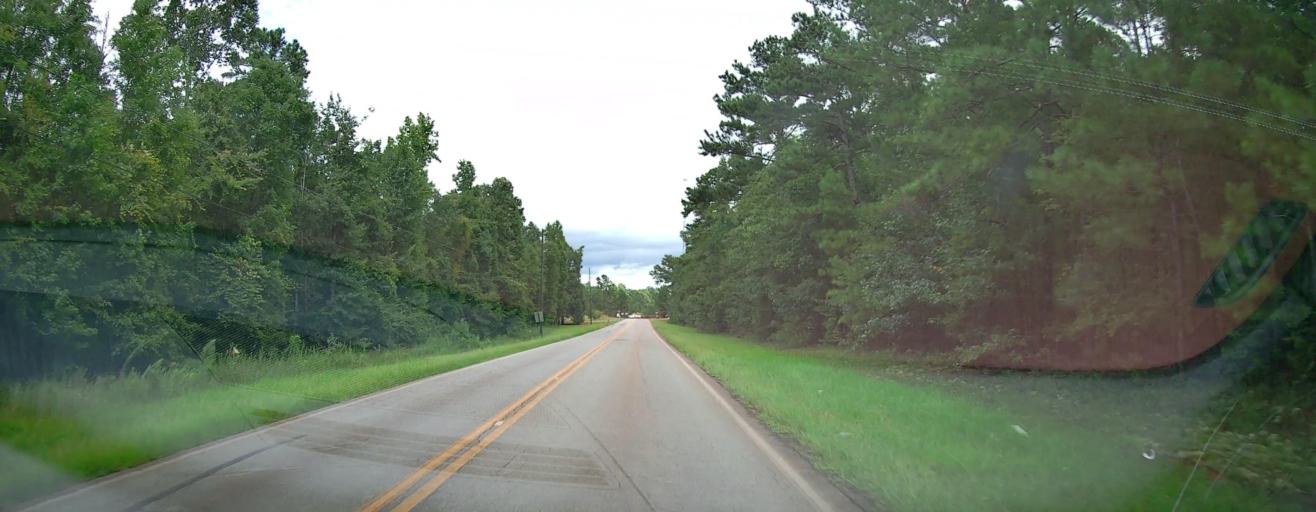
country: US
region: Georgia
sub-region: Twiggs County
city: Jeffersonville
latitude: 32.7646
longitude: -83.4834
